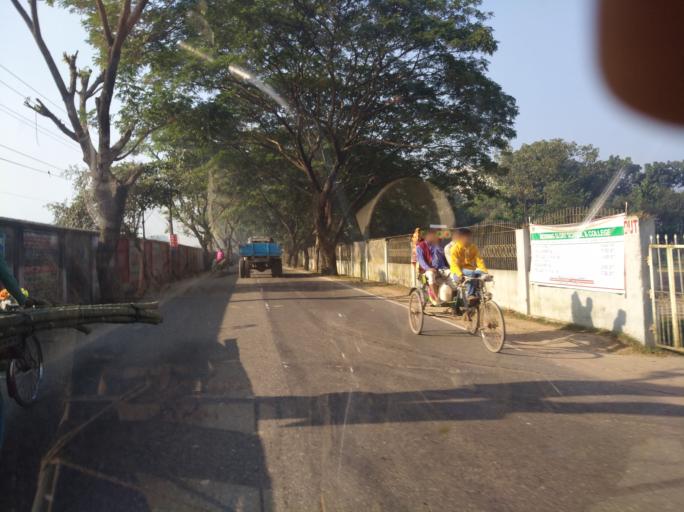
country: BD
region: Dhaka
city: Tungi
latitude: 23.9004
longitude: 90.2756
